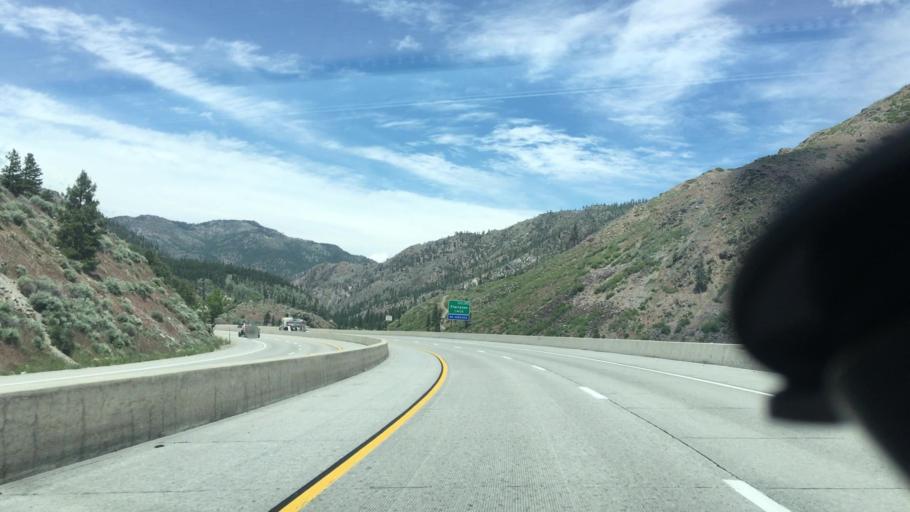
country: US
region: Nevada
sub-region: Washoe County
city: Incline Village
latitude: 39.3807
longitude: -120.0225
